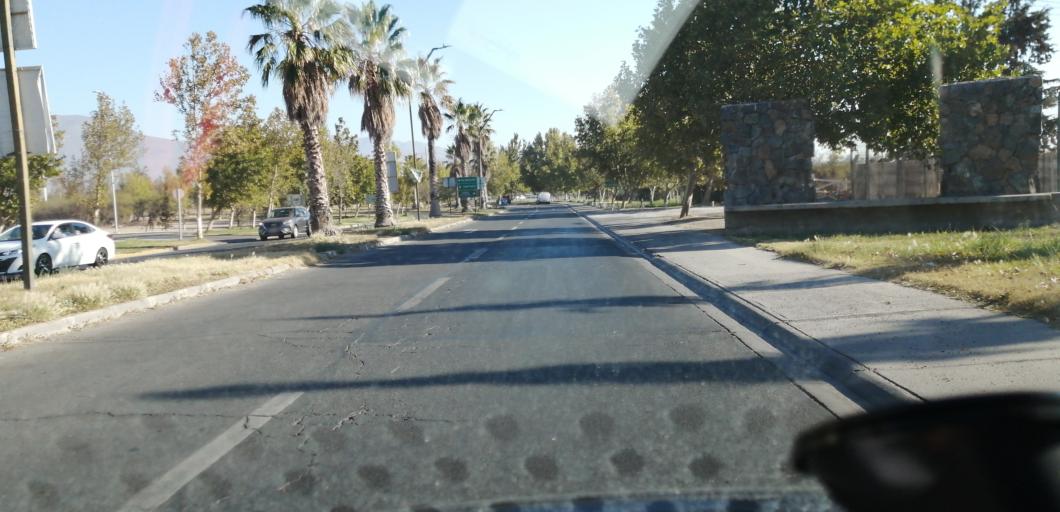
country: CL
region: Santiago Metropolitan
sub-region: Provincia de Santiago
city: Lo Prado
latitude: -33.4455
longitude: -70.8455
